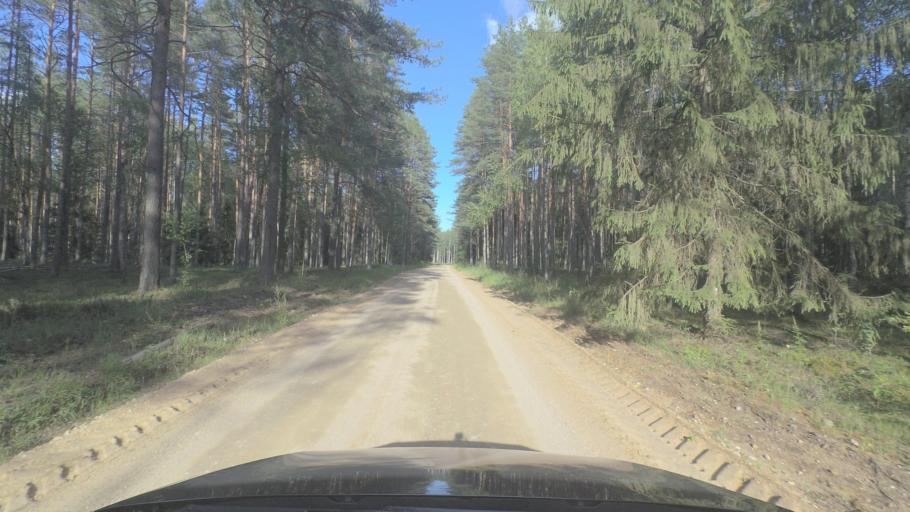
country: LT
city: Pabrade
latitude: 55.1550
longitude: 25.7933
